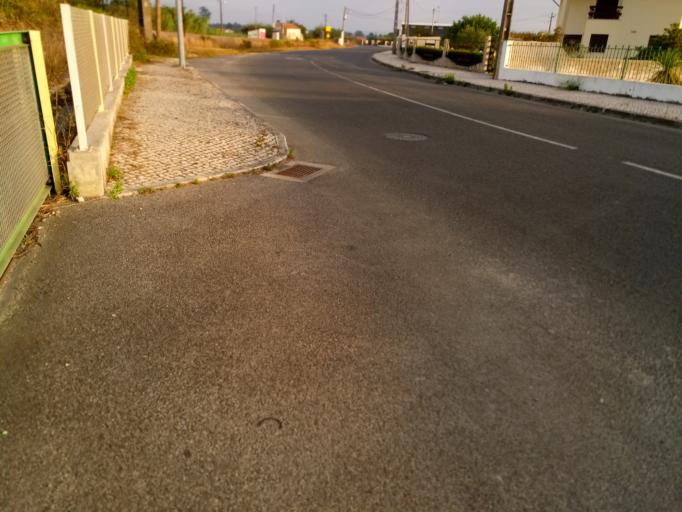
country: PT
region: Leiria
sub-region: Caldas da Rainha
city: Caldas da Rainha
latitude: 39.4159
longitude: -9.1420
